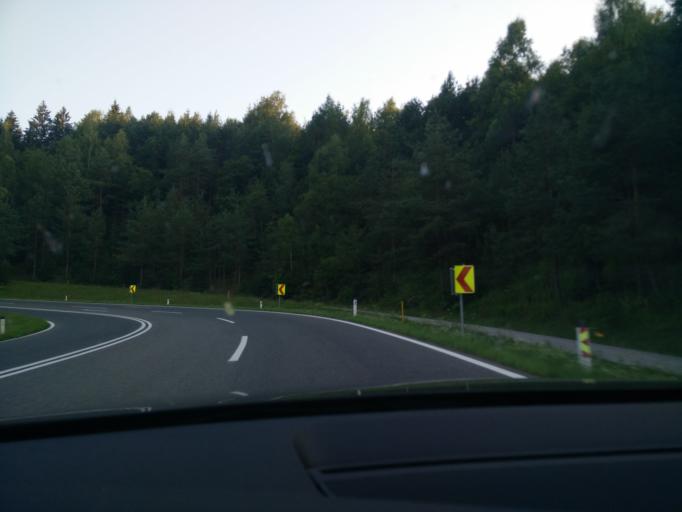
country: AT
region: Carinthia
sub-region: Villach Stadt
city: Villach
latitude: 46.5942
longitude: 13.8842
